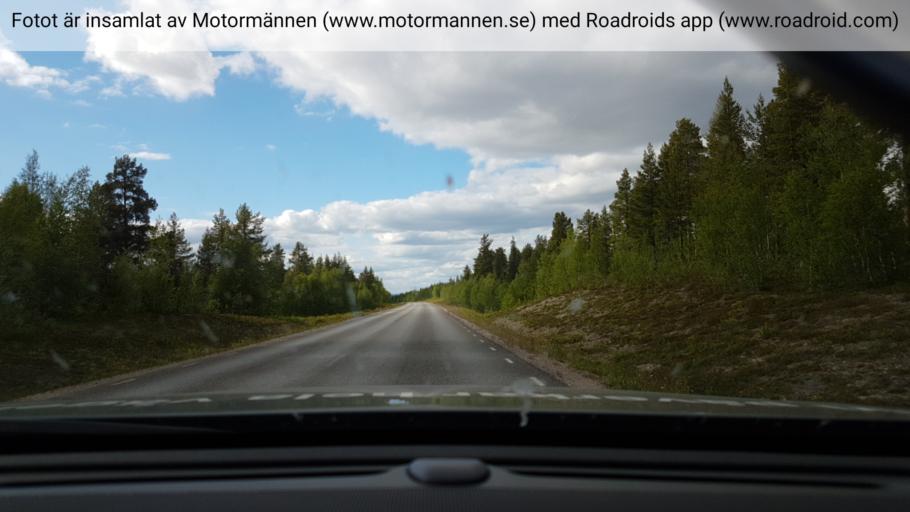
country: SE
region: Norrbotten
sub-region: Arjeplogs Kommun
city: Arjeplog
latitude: 66.1841
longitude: 17.3086
